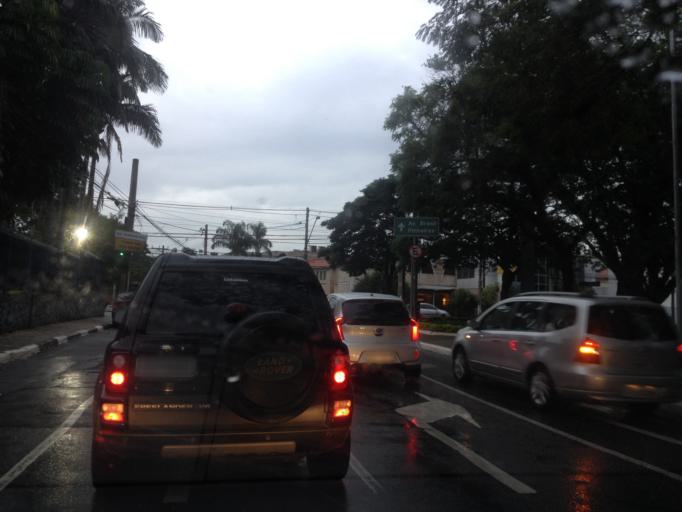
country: BR
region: Sao Paulo
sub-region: Sao Paulo
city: Sao Paulo
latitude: -23.5809
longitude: -46.6639
